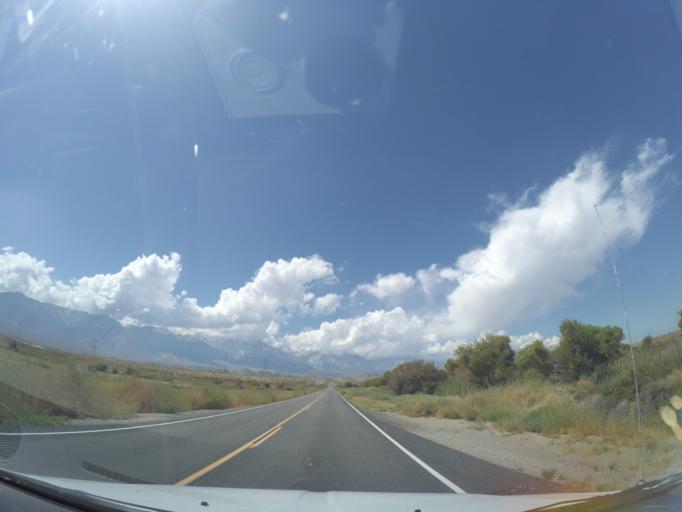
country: US
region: California
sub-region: Inyo County
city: Lone Pine
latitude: 36.5746
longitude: -118.0112
